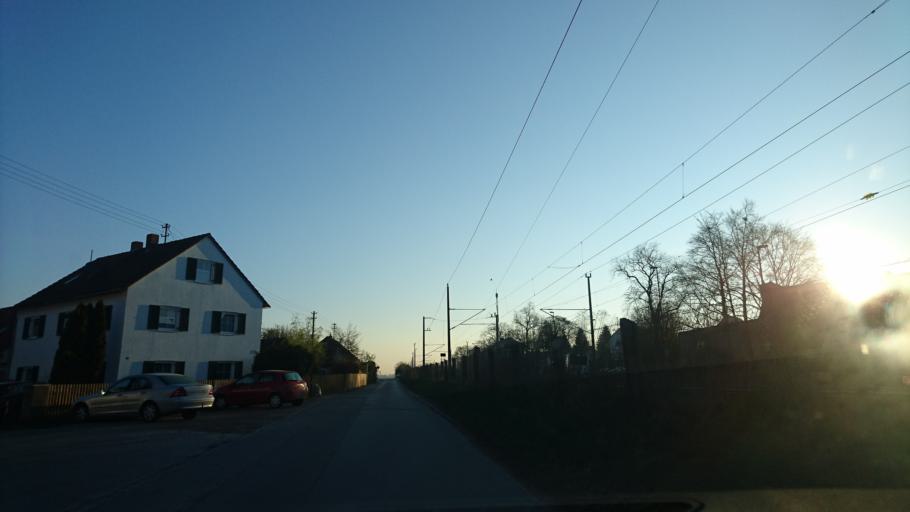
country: DE
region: Bavaria
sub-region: Swabia
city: Diedorf
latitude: 48.3552
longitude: 10.7755
